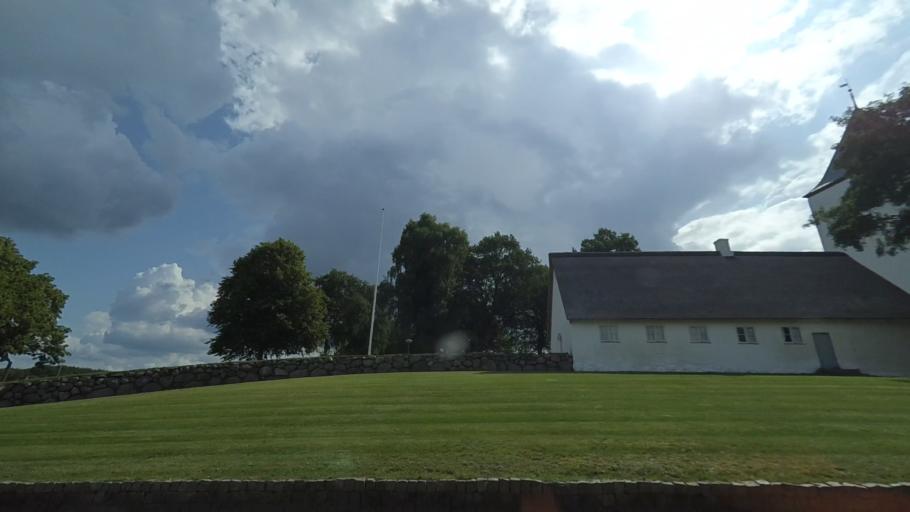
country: DK
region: Central Jutland
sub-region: Norddjurs Kommune
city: Allingabro
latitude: 56.4986
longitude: 10.3376
